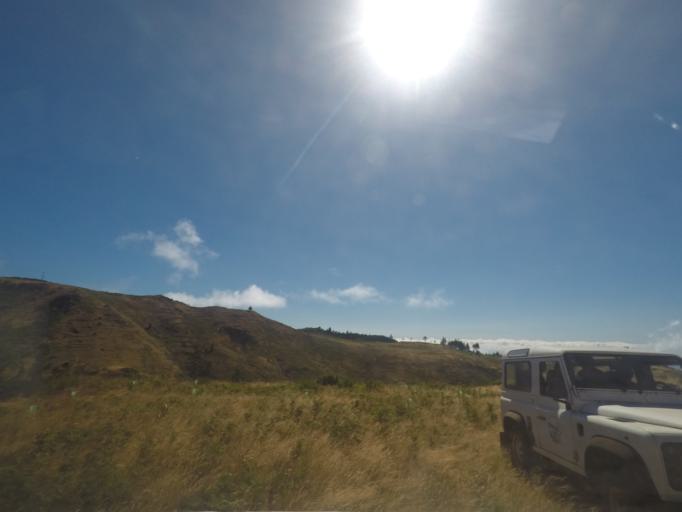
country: PT
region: Madeira
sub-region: Funchal
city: Nossa Senhora do Monte
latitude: 32.7116
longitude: -16.9049
